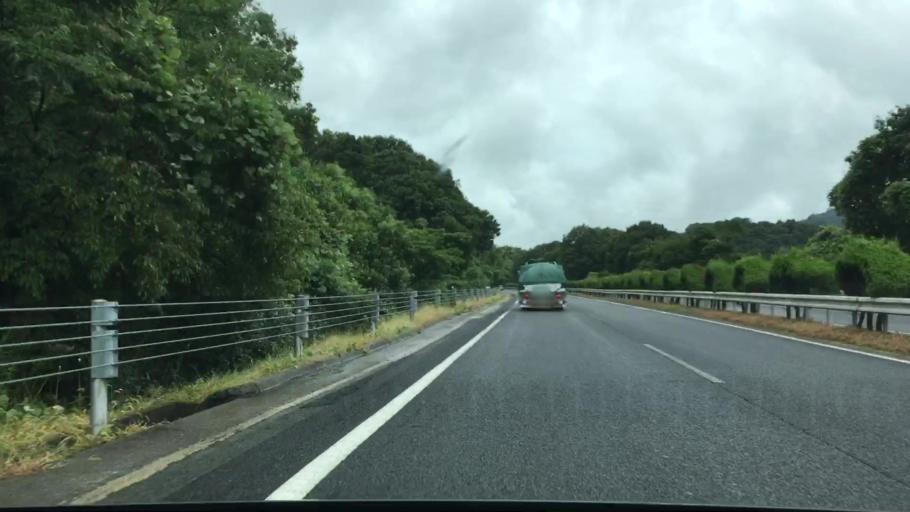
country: JP
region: Hyogo
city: Himeji
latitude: 34.9542
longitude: 134.7249
